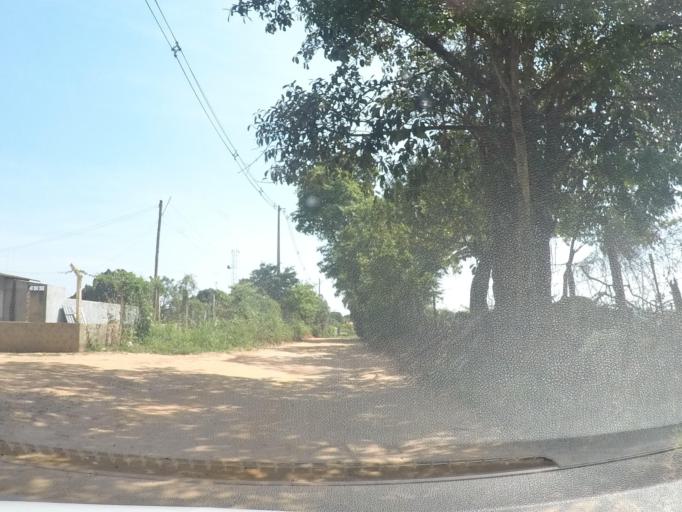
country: BR
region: Sao Paulo
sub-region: Sumare
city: Sumare
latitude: -22.8792
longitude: -47.2886
